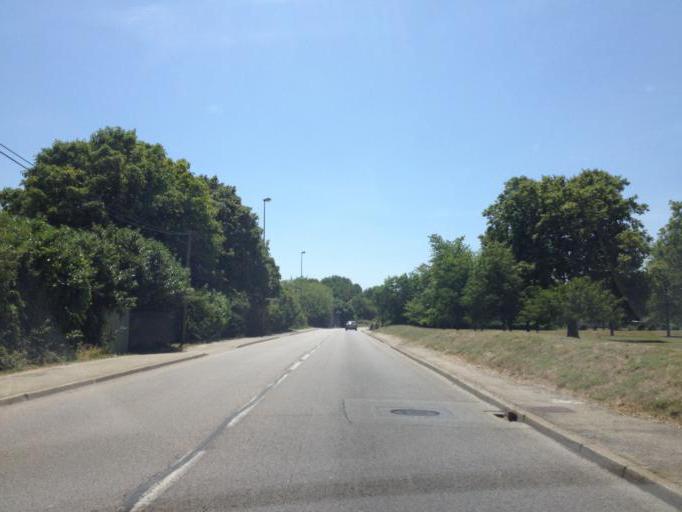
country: FR
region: Rhone-Alpes
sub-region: Departement de l'Ardeche
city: Guilherand-Granges
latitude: 44.9274
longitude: 4.8826
